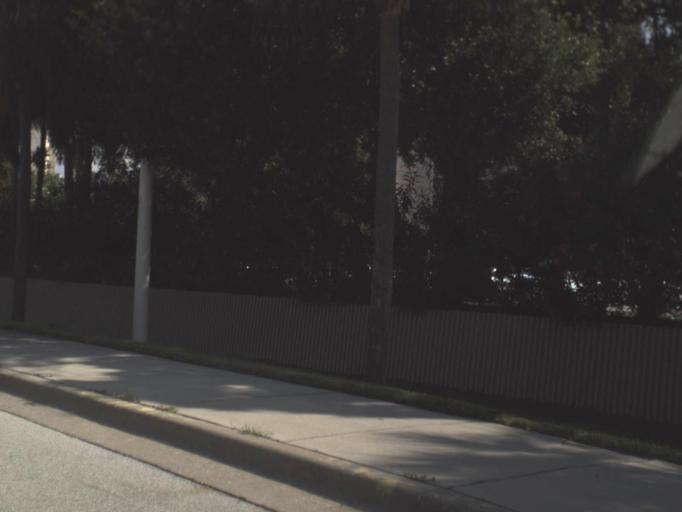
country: US
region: Florida
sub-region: Pinellas County
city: Treasure Island
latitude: 27.7560
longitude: -82.7583
